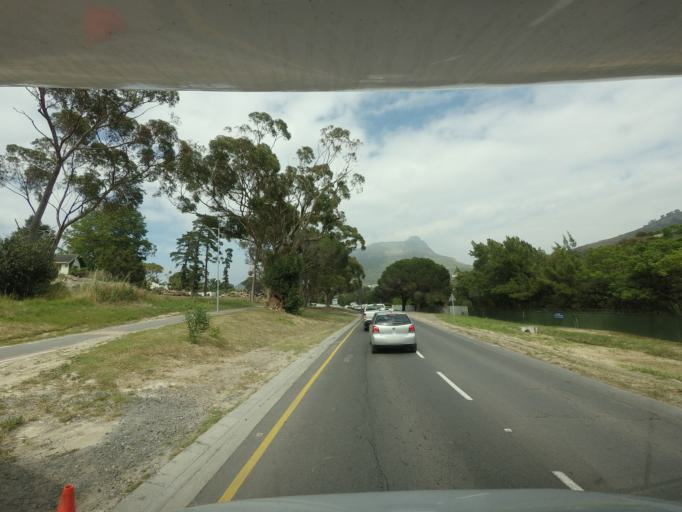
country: ZA
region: Western Cape
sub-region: City of Cape Town
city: Constantia
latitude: -34.0249
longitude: 18.3611
